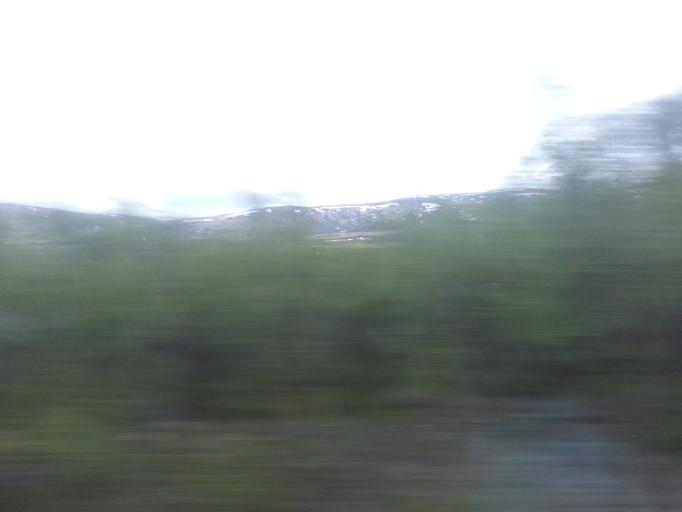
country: NO
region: Oppland
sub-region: Dovre
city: Dovre
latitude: 62.1968
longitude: 9.5048
